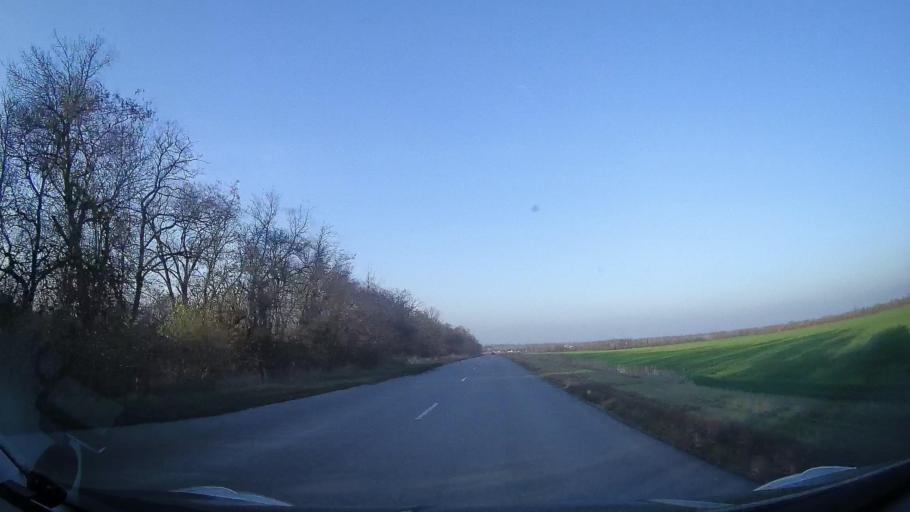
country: RU
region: Rostov
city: Kirovskaya
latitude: 47.0192
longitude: 39.9788
